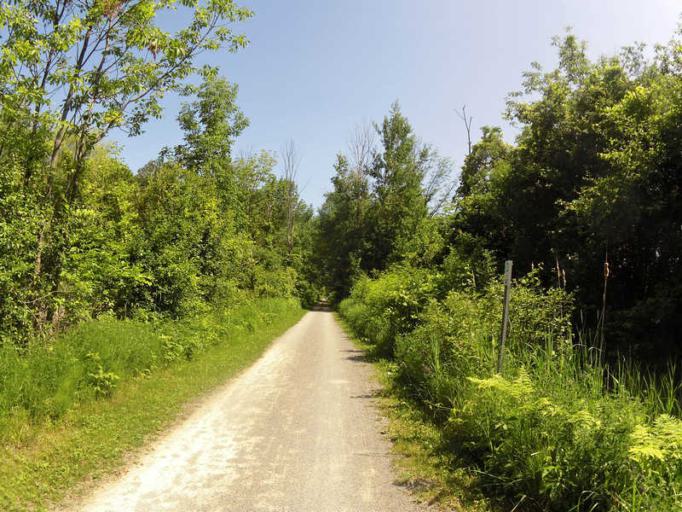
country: CA
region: Ontario
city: Peterborough
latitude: 44.3896
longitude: -78.2671
